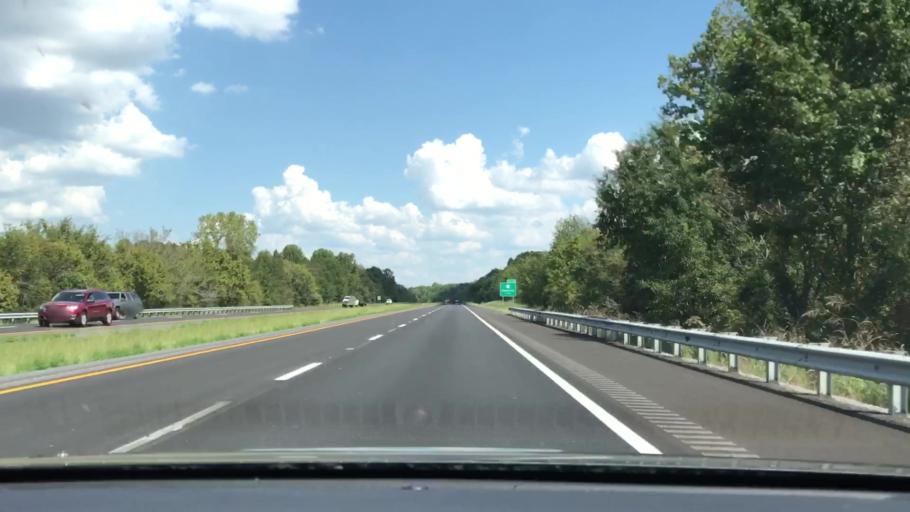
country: US
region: Kentucky
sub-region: Lyon County
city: Eddyville
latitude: 37.0915
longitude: -88.0524
